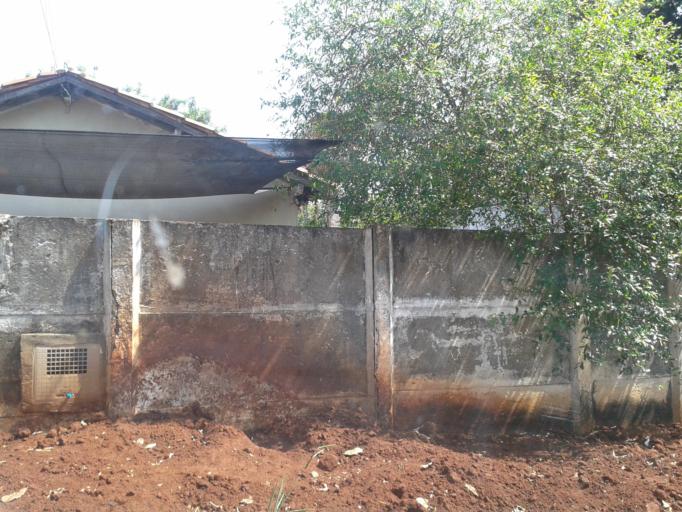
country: BR
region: Minas Gerais
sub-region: Ituiutaba
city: Ituiutaba
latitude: -18.9679
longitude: -49.4859
